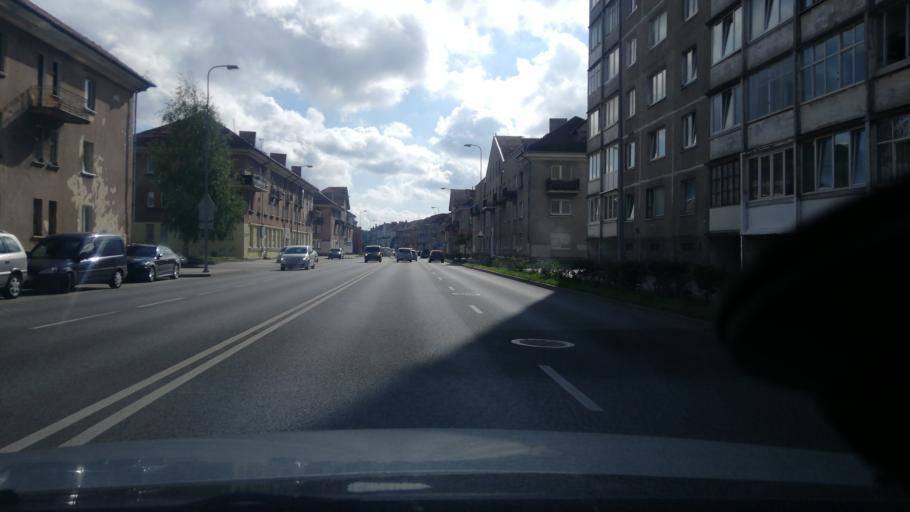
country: LT
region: Klaipedos apskritis
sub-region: Klaipeda
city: Klaipeda
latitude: 55.6803
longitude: 21.1515
